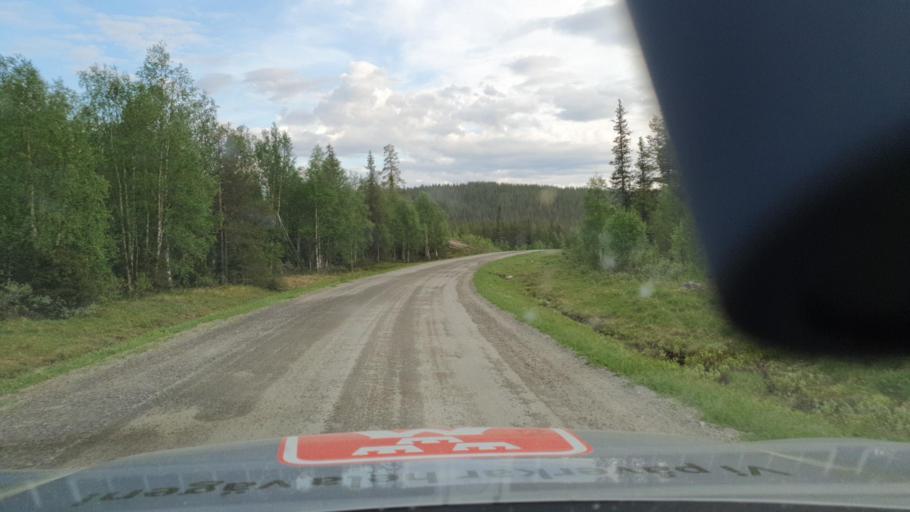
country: SE
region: Norrbotten
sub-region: Bodens Kommun
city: Boden
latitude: 66.6067
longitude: 21.3534
